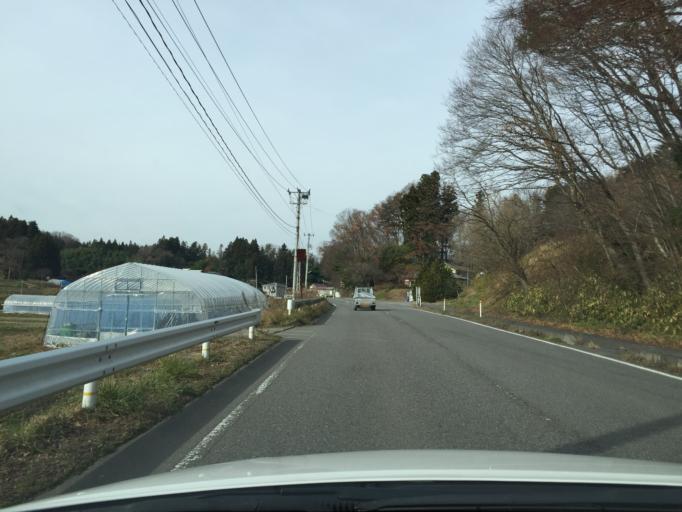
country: JP
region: Fukushima
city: Funehikimachi-funehiki
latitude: 37.4067
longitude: 140.5910
